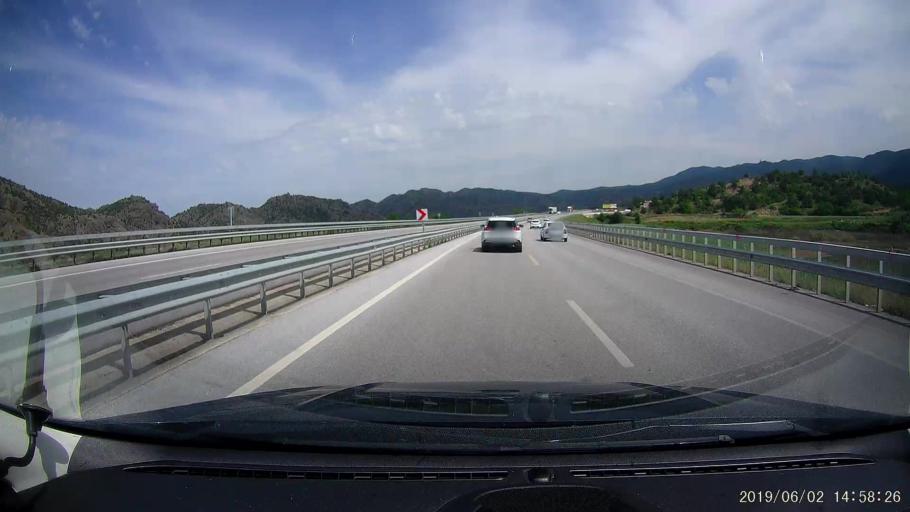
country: TR
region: Corum
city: Osmancik
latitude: 40.9824
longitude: 34.6755
